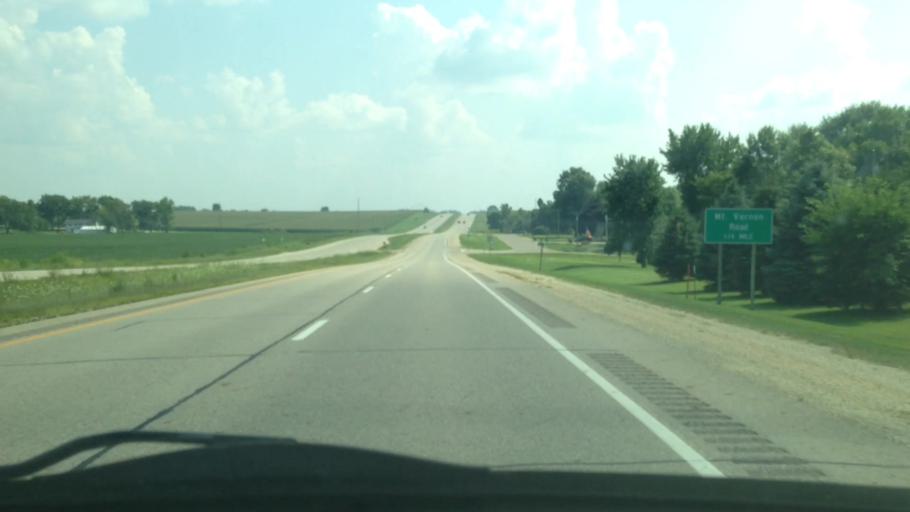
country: US
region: Iowa
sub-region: Bremer County
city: Denver
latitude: 42.5896
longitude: -92.3374
